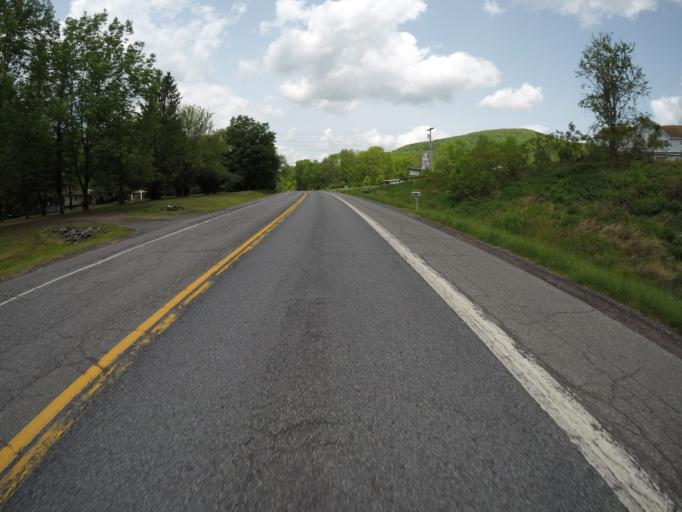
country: US
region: New York
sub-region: Delaware County
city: Stamford
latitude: 42.2481
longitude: -74.5963
